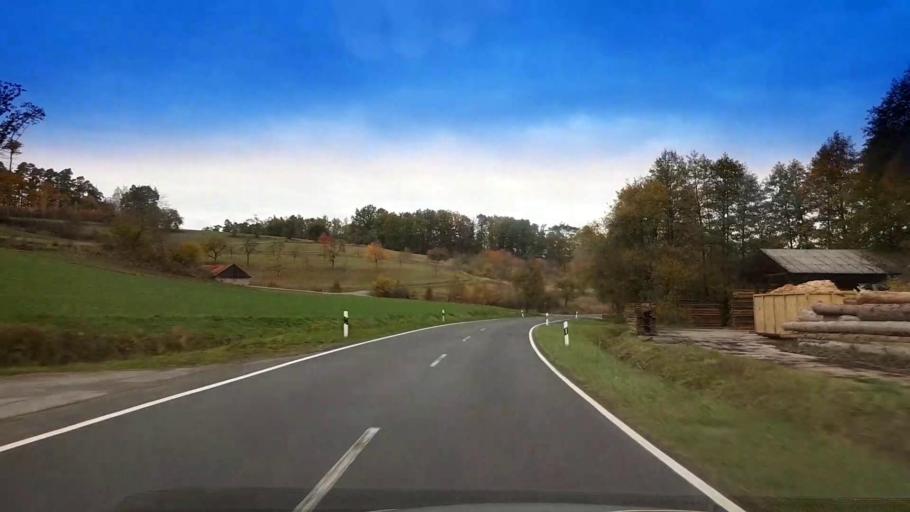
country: DE
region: Bavaria
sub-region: Regierungsbezirk Unterfranken
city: Stettfeld
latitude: 49.9500
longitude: 10.7049
